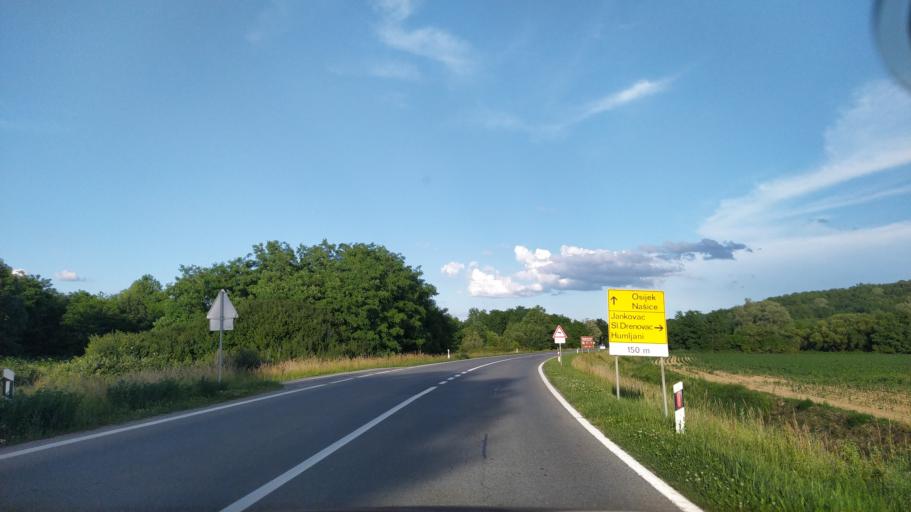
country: HR
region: Virovitick-Podravska
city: Cacinci
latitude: 45.6020
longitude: 17.8308
